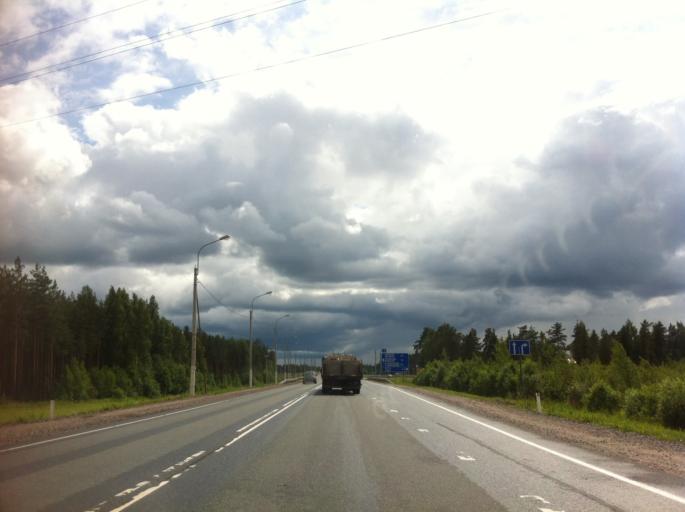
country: RU
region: Leningrad
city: Luga
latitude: 58.7369
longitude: 29.8877
